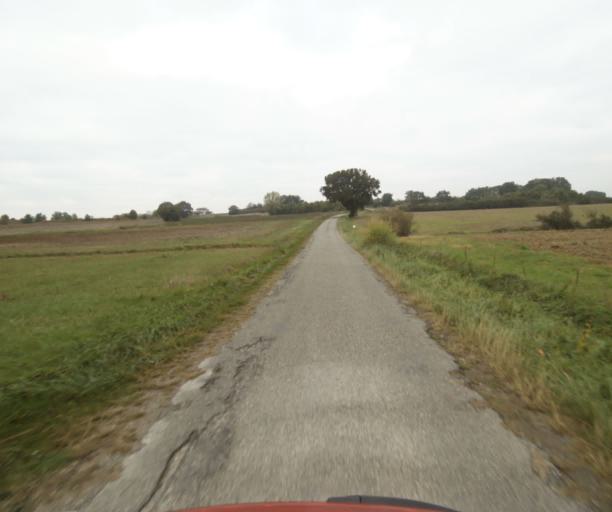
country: FR
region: Midi-Pyrenees
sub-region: Departement du Tarn-et-Garonne
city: Verdun-sur-Garonne
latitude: 43.8165
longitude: 1.2065
